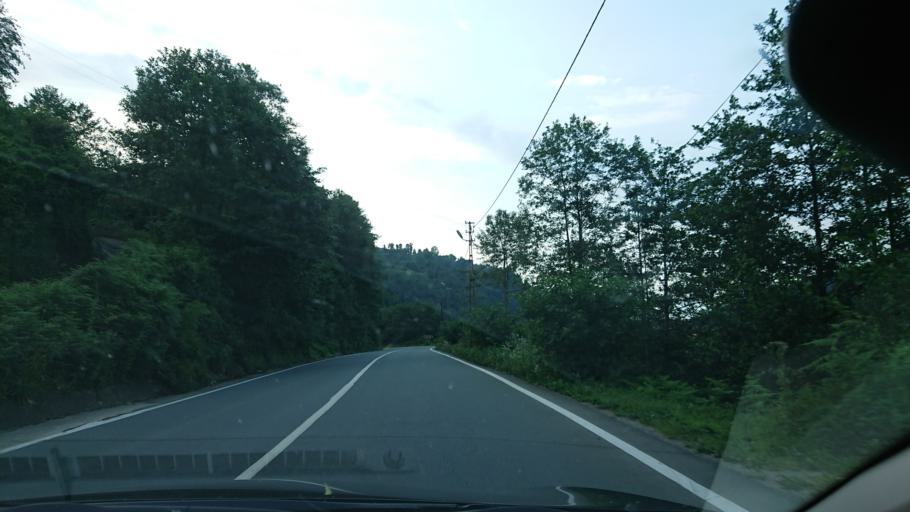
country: TR
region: Rize
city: Cayeli
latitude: 41.0679
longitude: 40.7135
